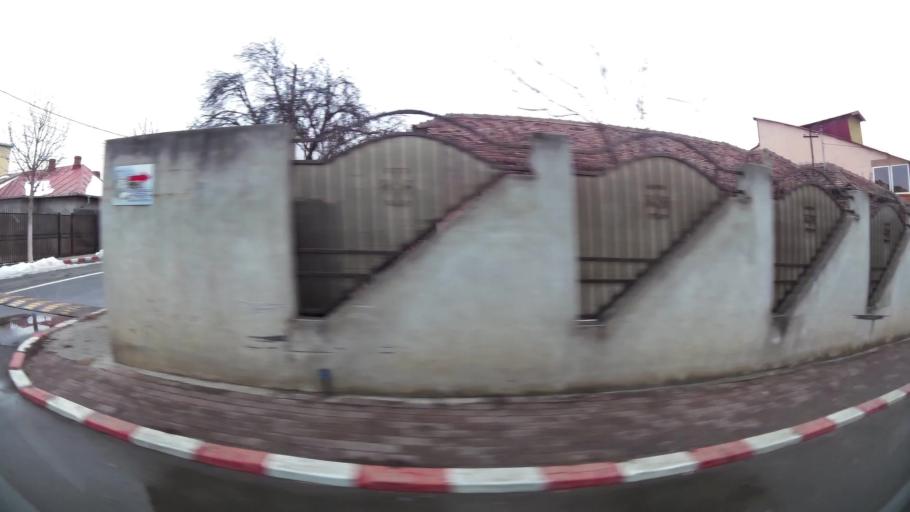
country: RO
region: Ilfov
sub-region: Voluntari City
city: Voluntari
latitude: 44.4915
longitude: 26.1818
